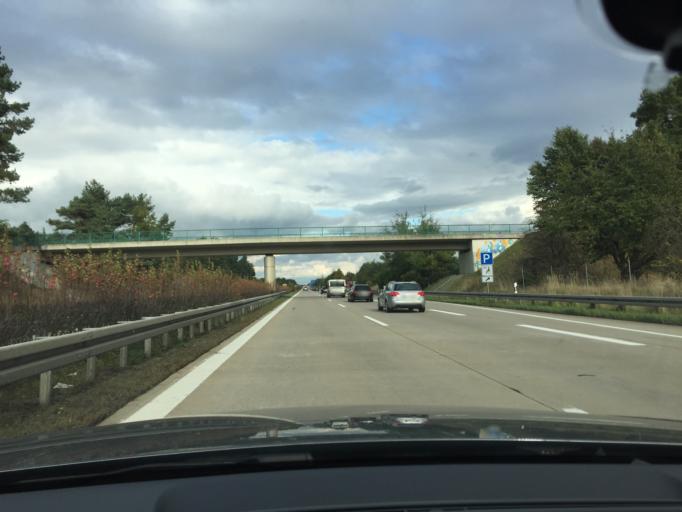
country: DE
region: Brandenburg
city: Ruhland
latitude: 51.4555
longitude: 13.8490
